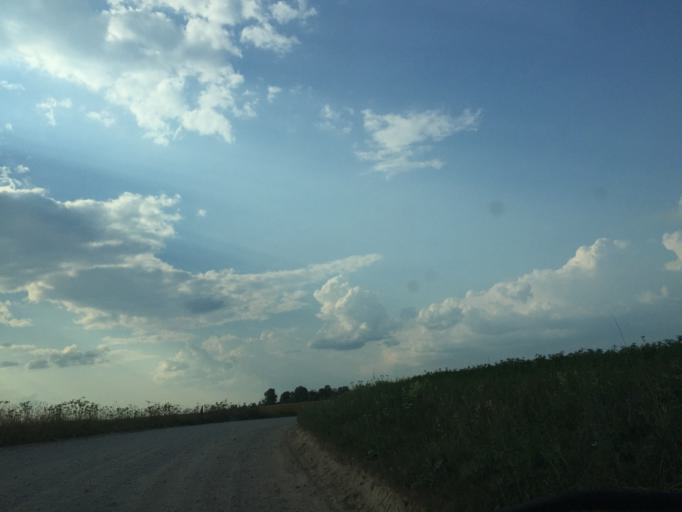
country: LT
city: Zagare
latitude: 56.4510
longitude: 23.1650
